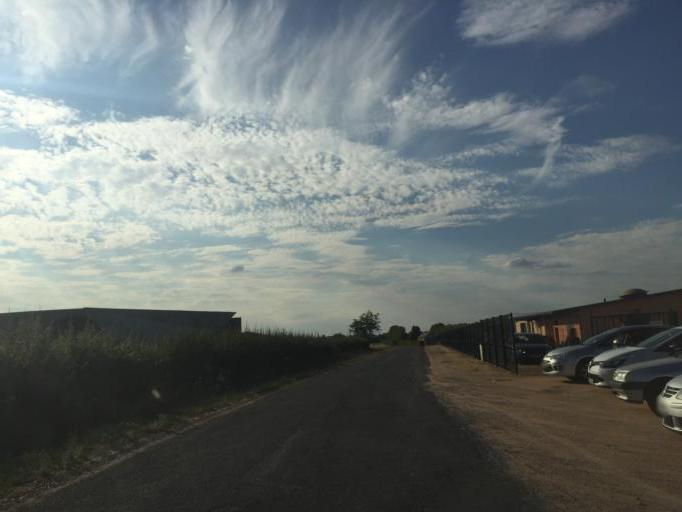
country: FR
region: Auvergne
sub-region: Departement de l'Allier
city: Toulon-sur-Allier
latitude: 46.5351
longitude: 3.3827
